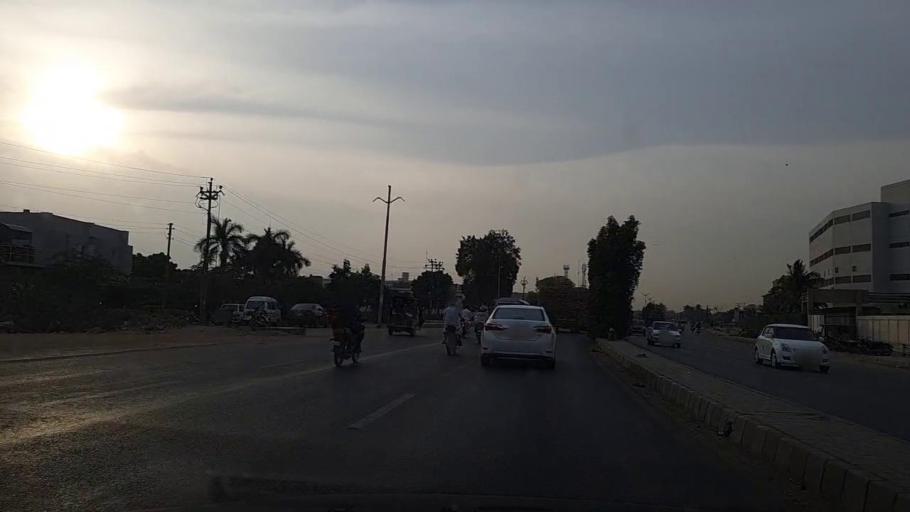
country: PK
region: Sindh
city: Malir Cantonment
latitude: 24.8532
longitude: 67.2478
